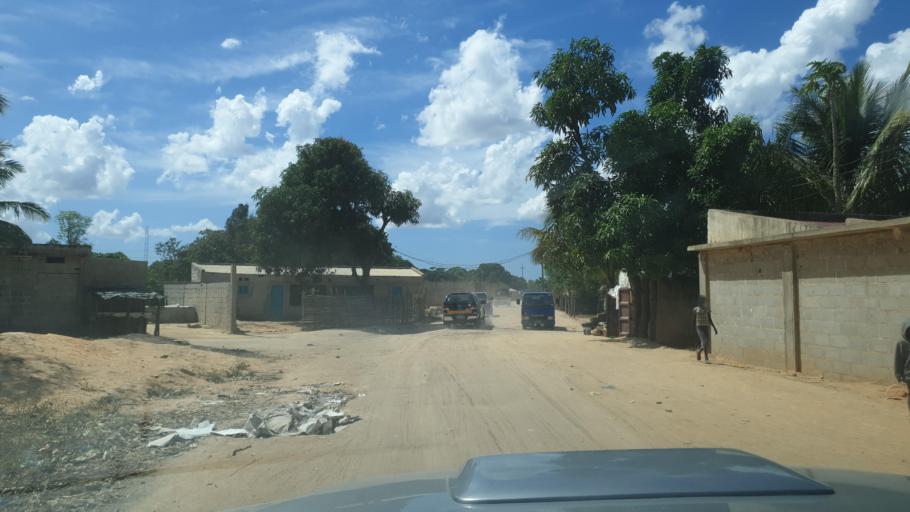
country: MZ
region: Nampula
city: Nacala
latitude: -14.5669
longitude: 40.6976
